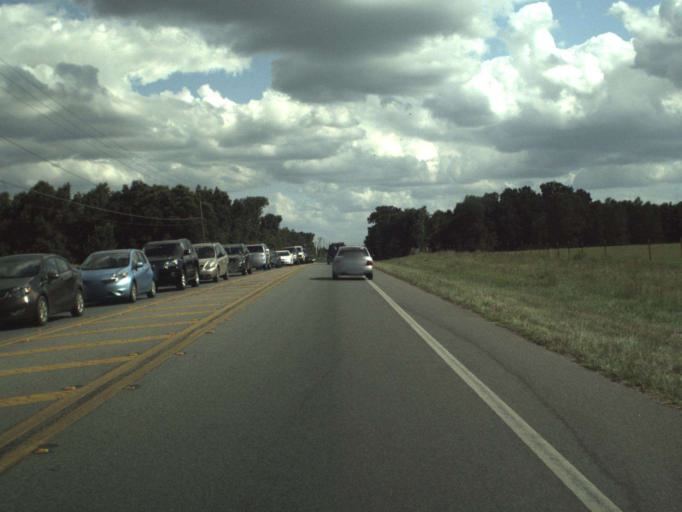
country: US
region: Florida
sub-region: Marion County
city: Silver Springs Shores
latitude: 29.1259
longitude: -82.0537
